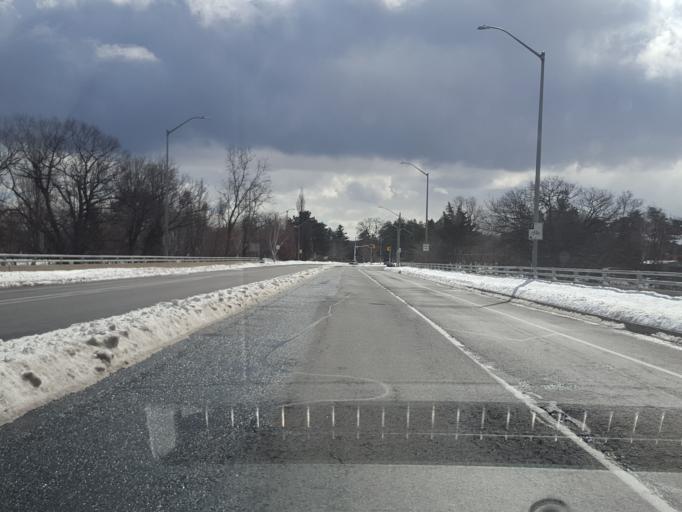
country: CA
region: Ontario
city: Hamilton
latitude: 43.2918
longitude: -79.8904
